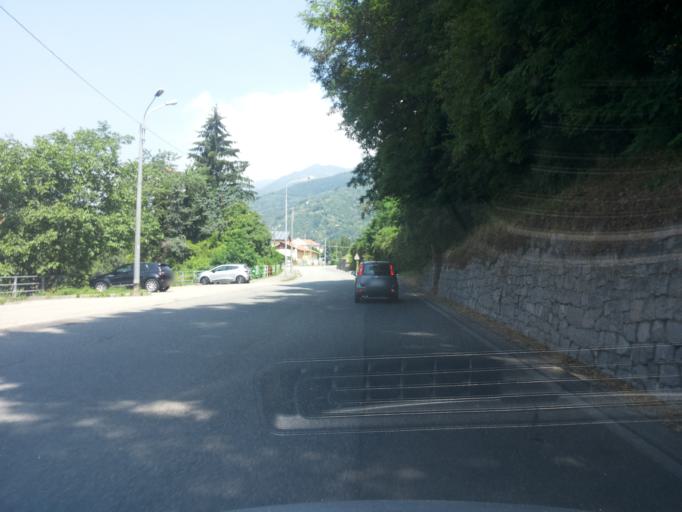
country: IT
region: Piedmont
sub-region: Provincia di Biella
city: Tavigliano
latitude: 45.6198
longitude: 8.0469
